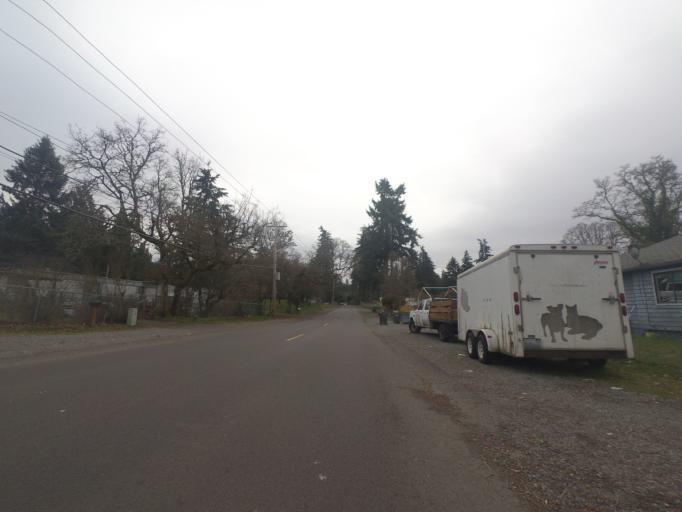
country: US
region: Washington
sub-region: Pierce County
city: McChord Air Force Base
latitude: 47.1238
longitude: -122.5273
